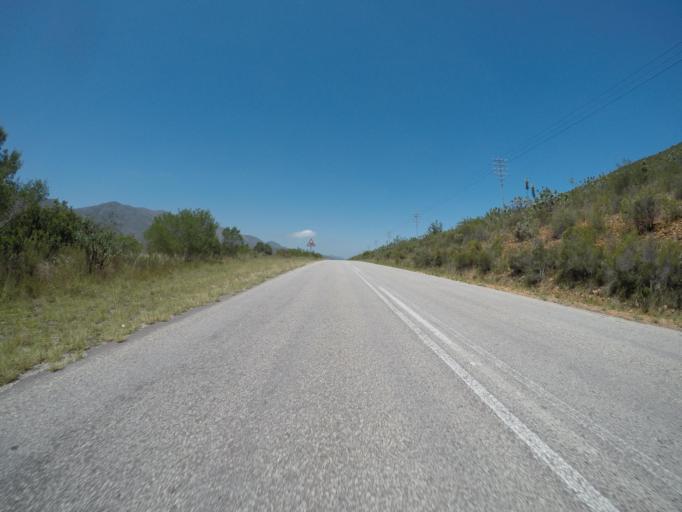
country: ZA
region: Eastern Cape
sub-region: Cacadu District Municipality
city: Kareedouw
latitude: -33.9059
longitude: 24.1447
